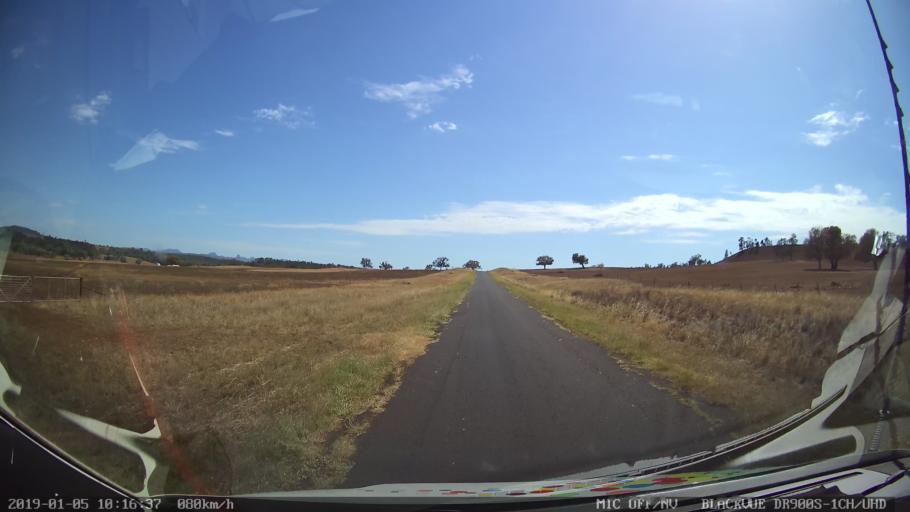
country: AU
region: New South Wales
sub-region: Gilgandra
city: Gilgandra
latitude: -31.5735
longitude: 148.9541
